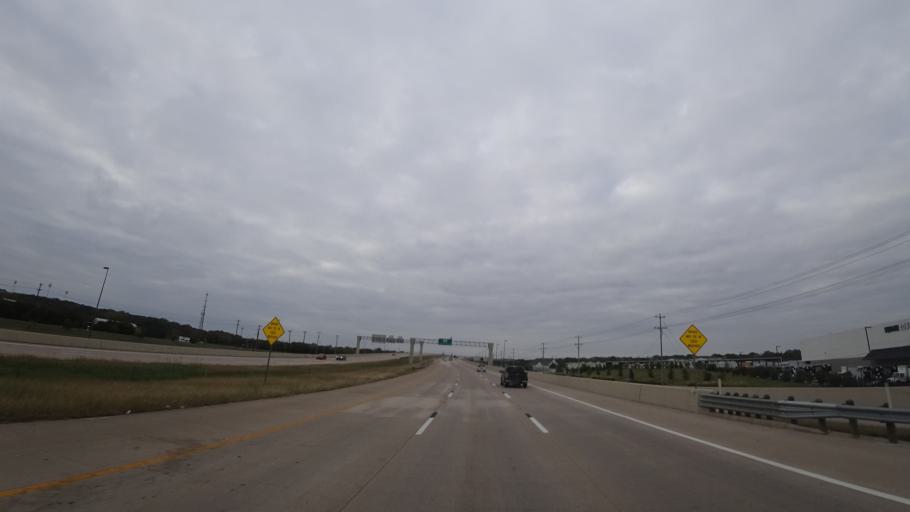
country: US
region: Texas
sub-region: Williamson County
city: Cedar Park
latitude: 30.4990
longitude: -97.8043
